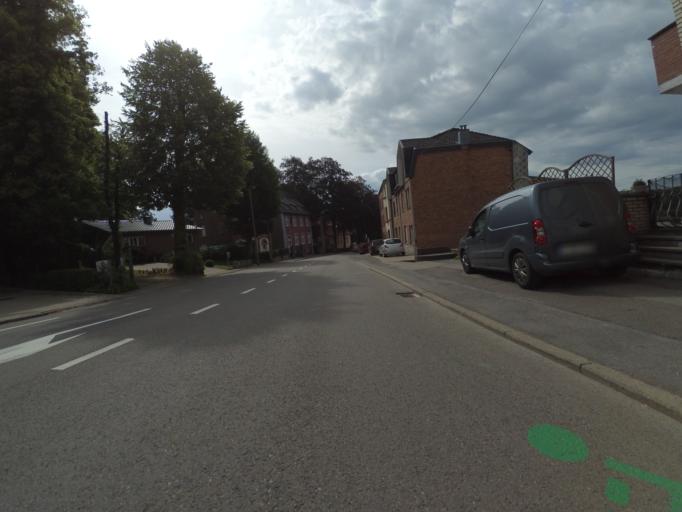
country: BE
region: Wallonia
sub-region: Province de Liege
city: La Calamine
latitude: 50.7159
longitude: 6.0164
